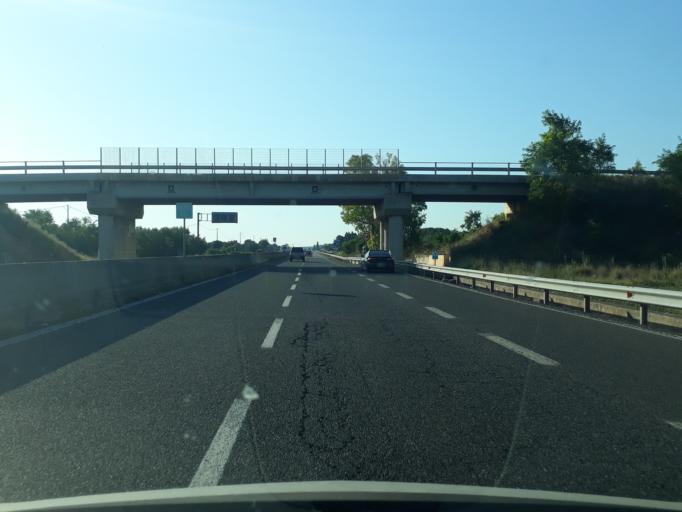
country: IT
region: Apulia
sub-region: Provincia di Brindisi
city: Carovigno
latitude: 40.7412
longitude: 17.7166
